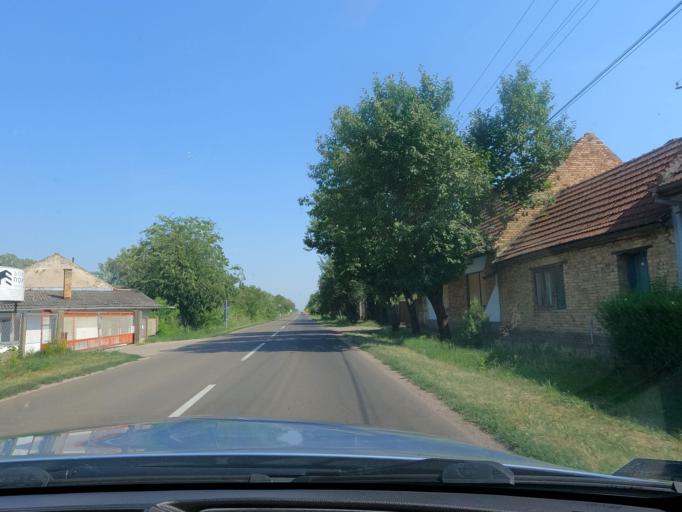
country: RS
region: Autonomna Pokrajina Vojvodina
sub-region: Severnobacki Okrug
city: Backa Topola
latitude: 45.8038
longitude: 19.6500
